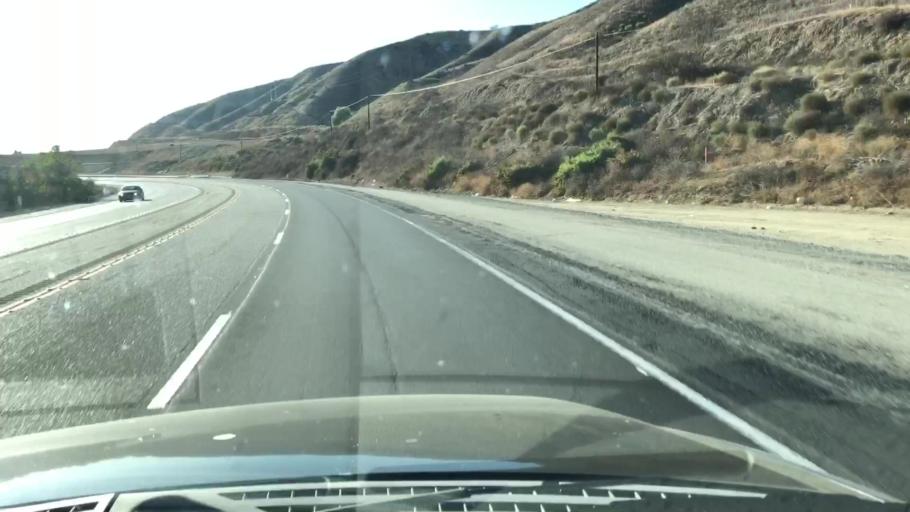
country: US
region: California
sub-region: Ventura County
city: Piru
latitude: 34.4105
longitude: -118.7278
